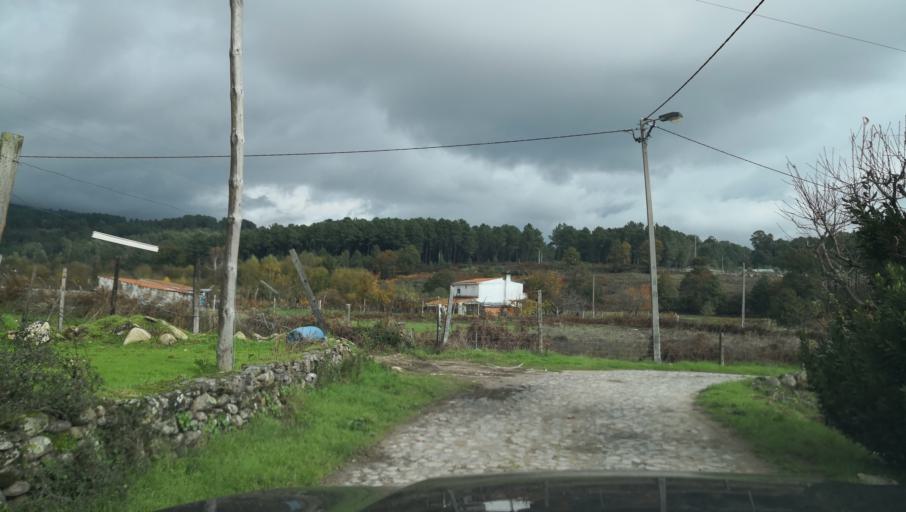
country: PT
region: Vila Real
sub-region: Vila Real
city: Vila Real
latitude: 41.3141
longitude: -7.7568
